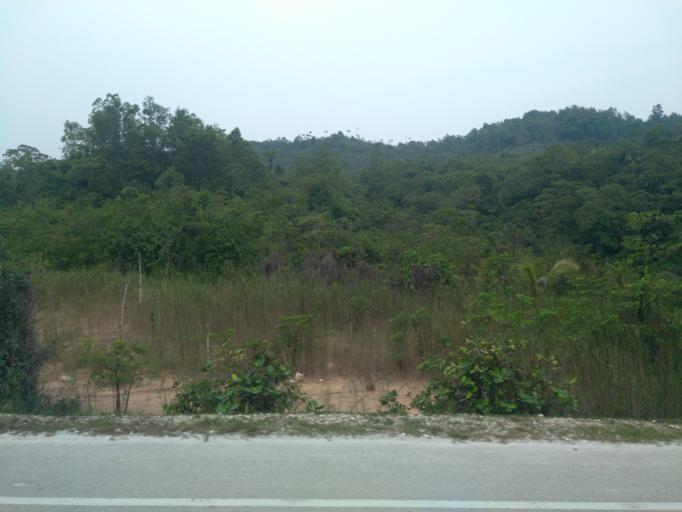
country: MY
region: Perak
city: Ipoh
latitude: 4.5469
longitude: 101.1604
